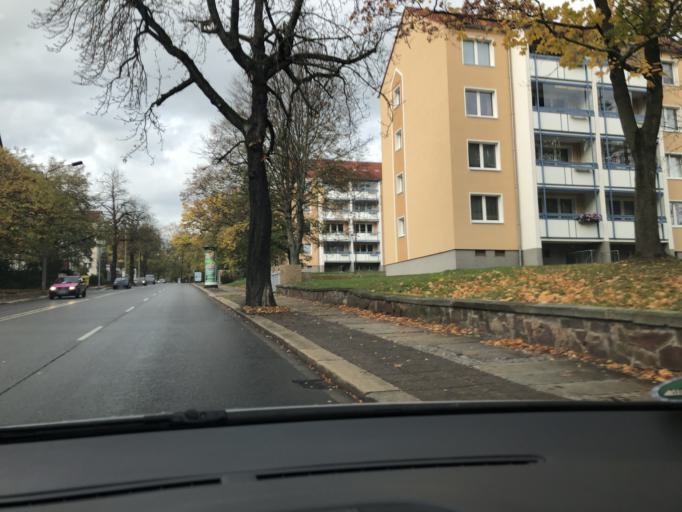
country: DE
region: Saxony
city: Chemnitz
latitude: 50.8303
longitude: 12.9100
